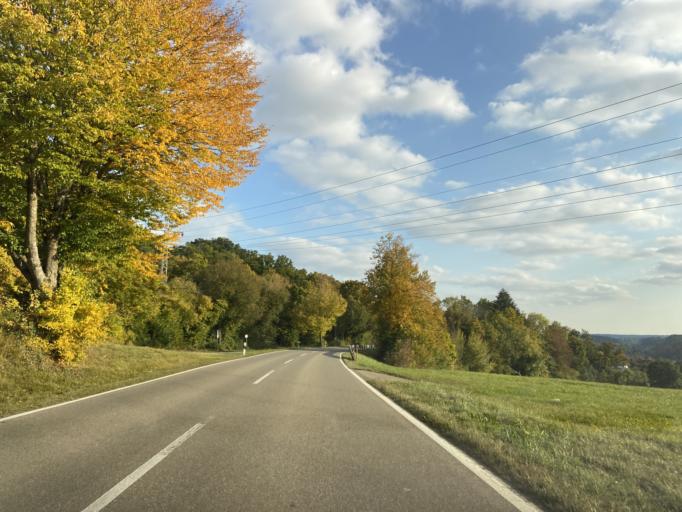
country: DE
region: Baden-Wuerttemberg
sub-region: Tuebingen Region
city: Scheer
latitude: 48.0820
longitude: 9.2921
